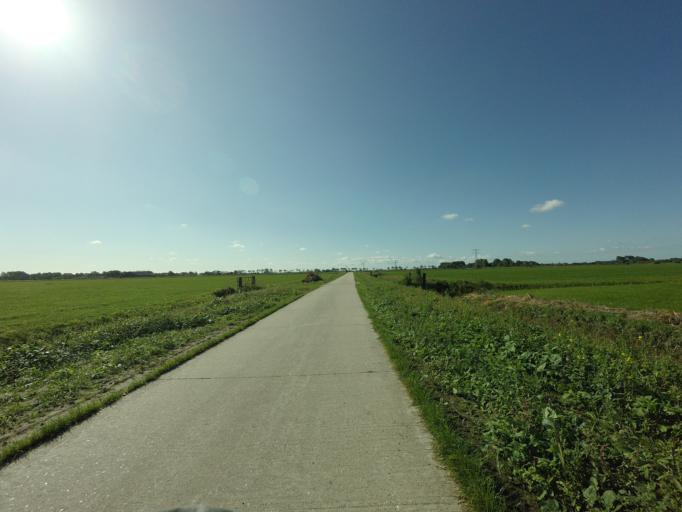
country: NL
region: Friesland
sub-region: Gemeente Leeuwarden
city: Wirdum
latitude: 53.1553
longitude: 5.7712
